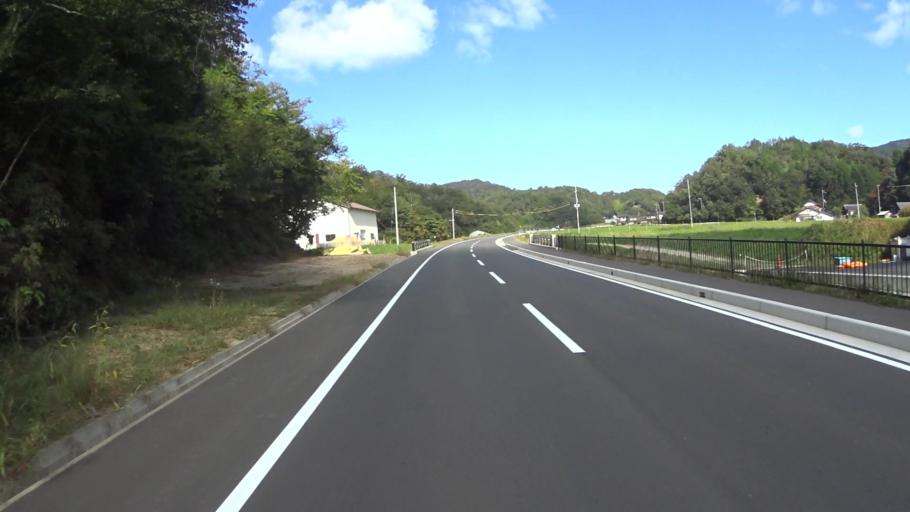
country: JP
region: Kyoto
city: Miyazu
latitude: 35.6112
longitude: 135.1336
